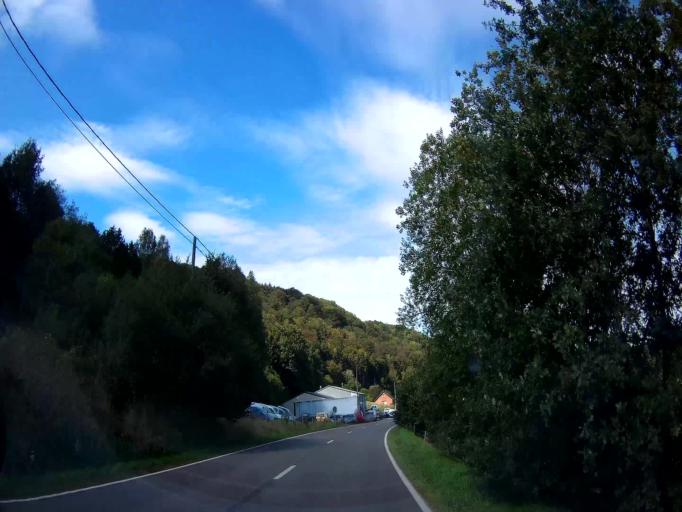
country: BE
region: Wallonia
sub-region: Province du Luxembourg
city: La Roche-en-Ardenne
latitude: 50.1964
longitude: 5.5363
